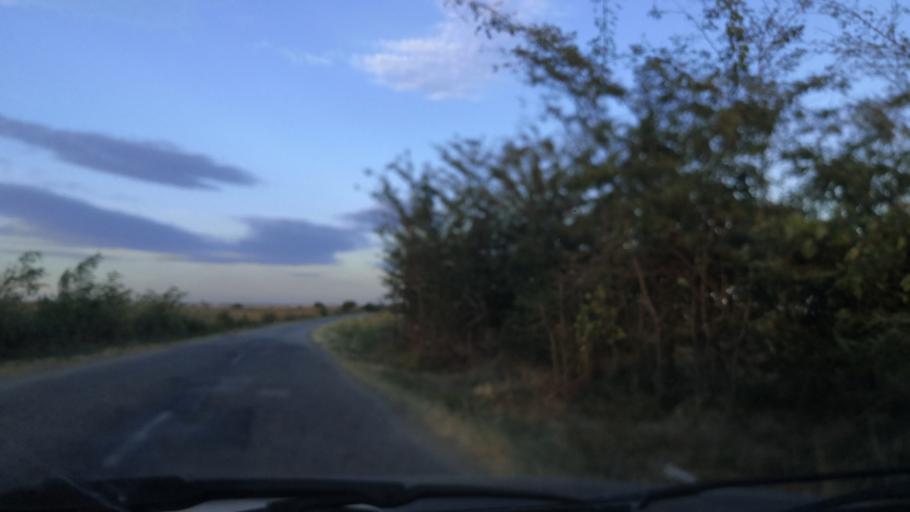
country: RO
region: Mehedinti
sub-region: Comuna Gruia
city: Izvoarele
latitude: 44.2635
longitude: 22.6461
